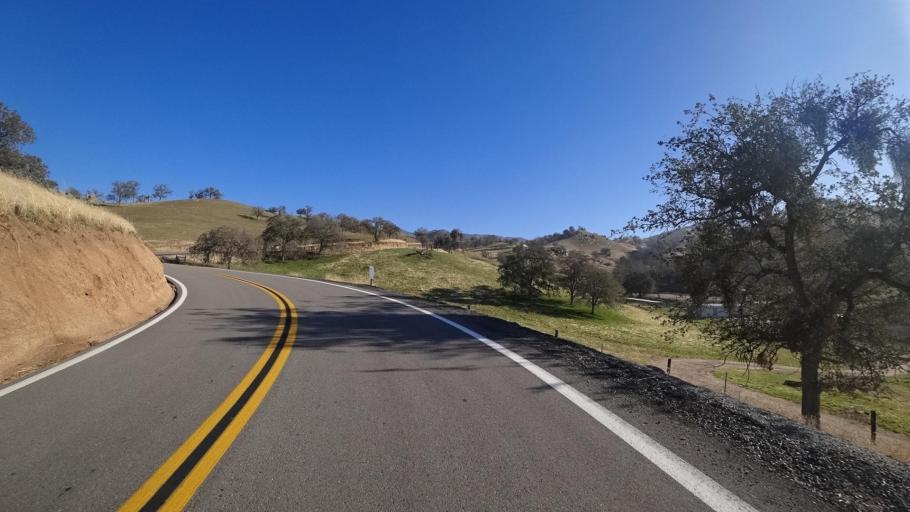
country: US
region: California
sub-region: Kern County
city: Alta Sierra
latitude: 35.7177
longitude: -118.8089
